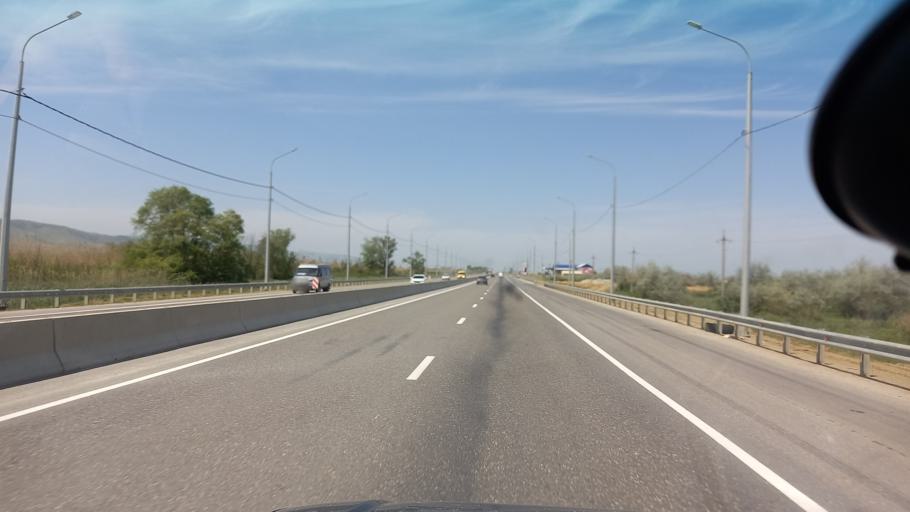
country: RU
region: Dagestan
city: Manas
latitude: 42.7376
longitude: 47.6613
